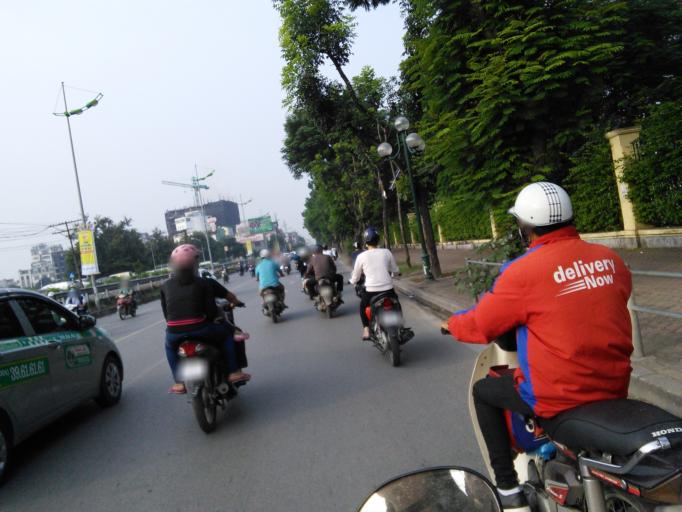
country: VN
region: Ha Noi
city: Hai BaTrung
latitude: 21.0116
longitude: 105.8414
